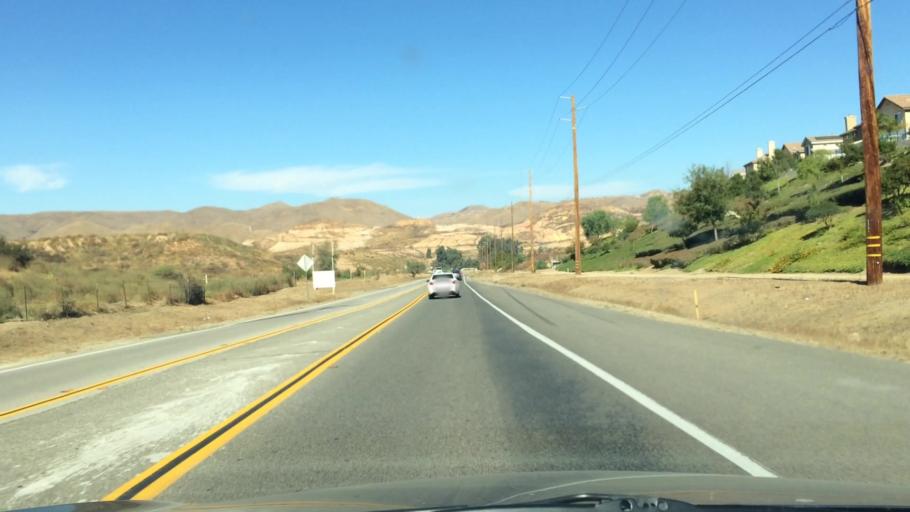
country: US
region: California
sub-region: Riverside County
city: Lake Elsinore
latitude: 33.7061
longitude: -117.3887
